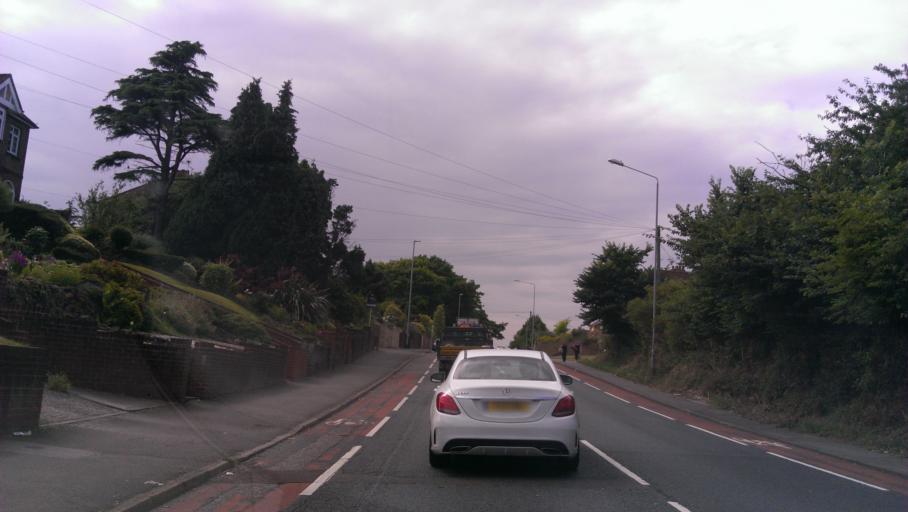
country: GB
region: England
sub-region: Kent
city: Sittingbourne
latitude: 51.3353
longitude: 0.7639
